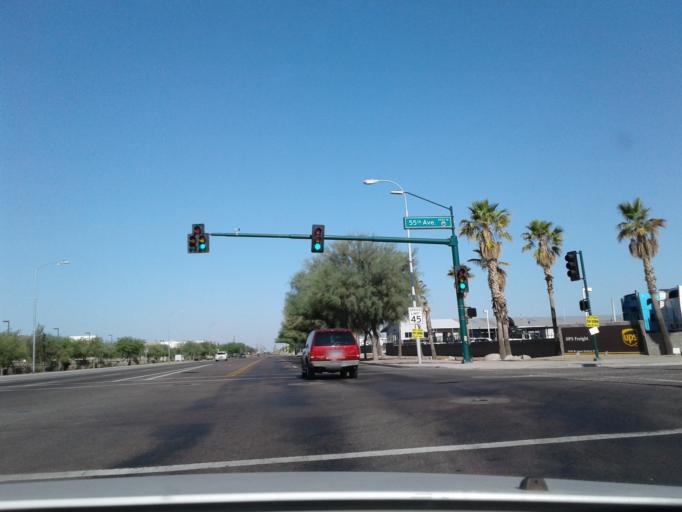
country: US
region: Arizona
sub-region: Maricopa County
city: Laveen
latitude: 33.4224
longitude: -112.1778
